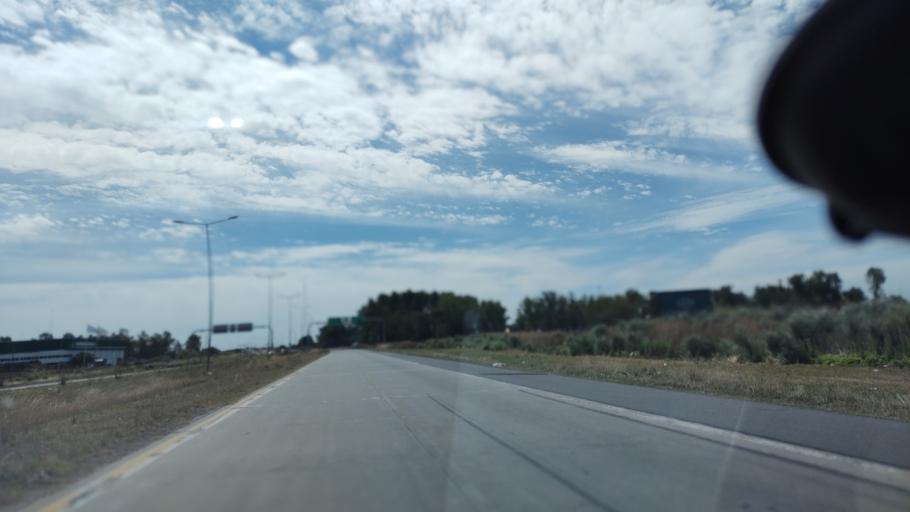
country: AR
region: Buenos Aires
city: Canuelas
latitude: -35.0343
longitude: -58.7206
